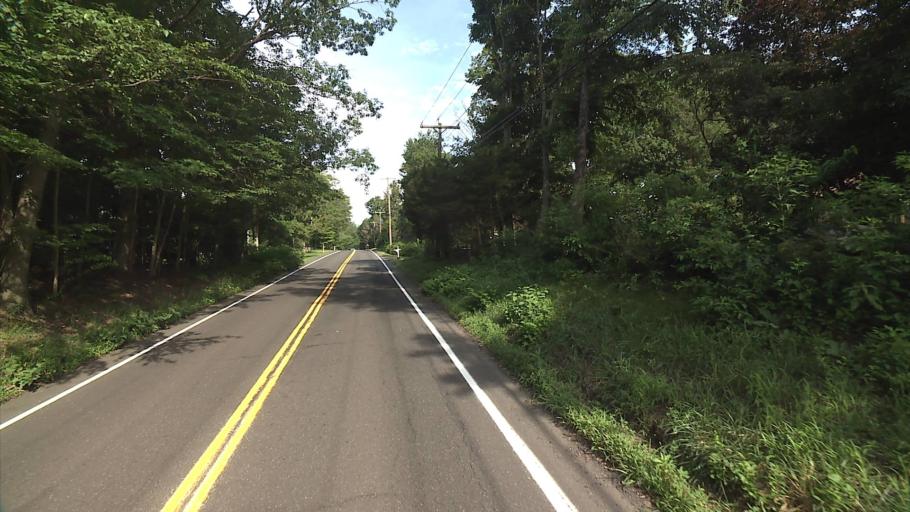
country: US
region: Connecticut
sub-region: New Haven County
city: Woodbridge
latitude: 41.3573
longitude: -73.0399
